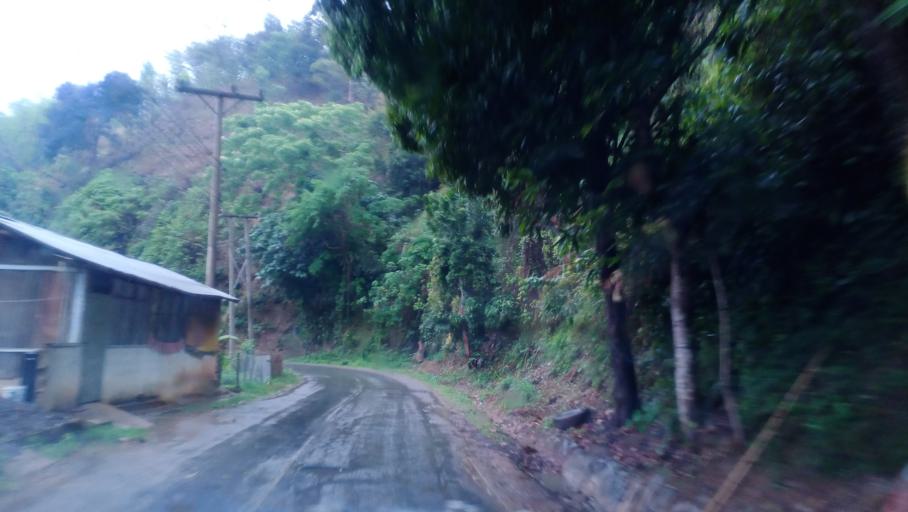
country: LA
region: Phongsali
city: Khoa
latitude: 21.0773
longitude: 102.5006
